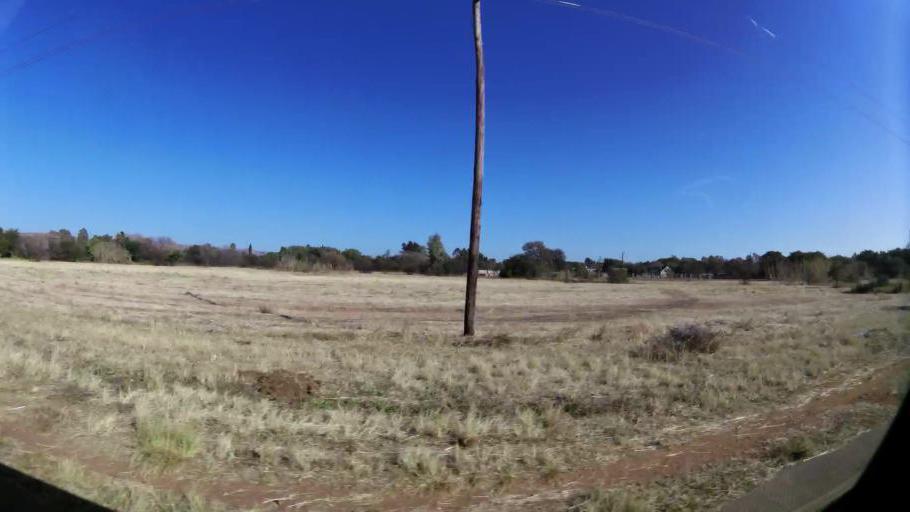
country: ZA
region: Gauteng
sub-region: City of Tshwane Metropolitan Municipality
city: Pretoria
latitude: -25.6628
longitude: 28.1321
